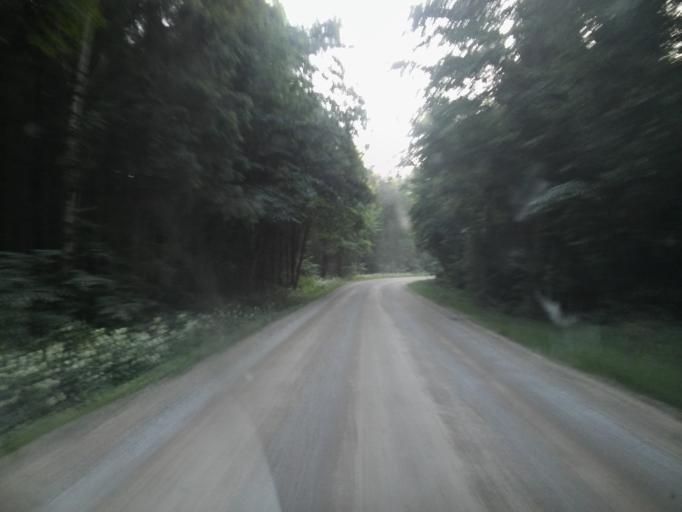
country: EE
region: Viljandimaa
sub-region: Abja vald
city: Abja-Paluoja
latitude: 58.2748
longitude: 25.3102
